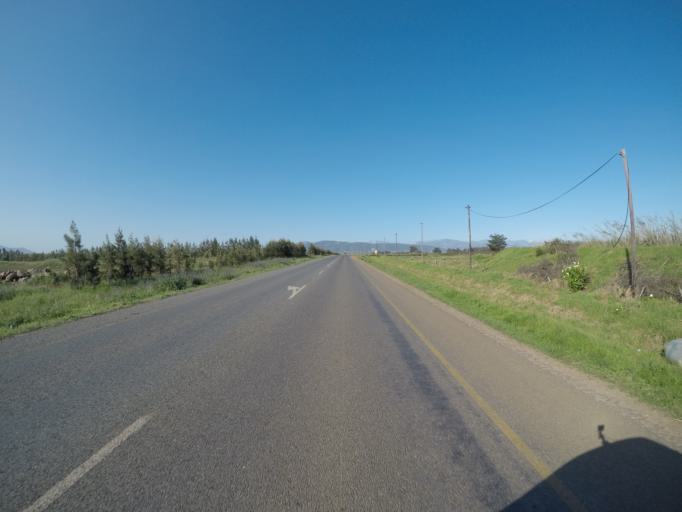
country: ZA
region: Western Cape
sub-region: City of Cape Town
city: Kraaifontein
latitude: -33.7653
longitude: 18.7922
